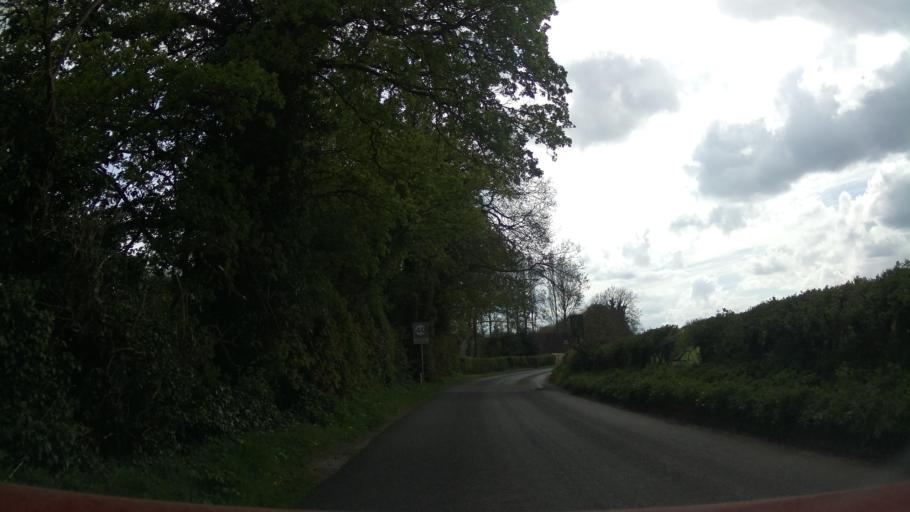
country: GB
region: England
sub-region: Hampshire
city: Abbotts Ann
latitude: 51.1074
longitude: -1.5022
